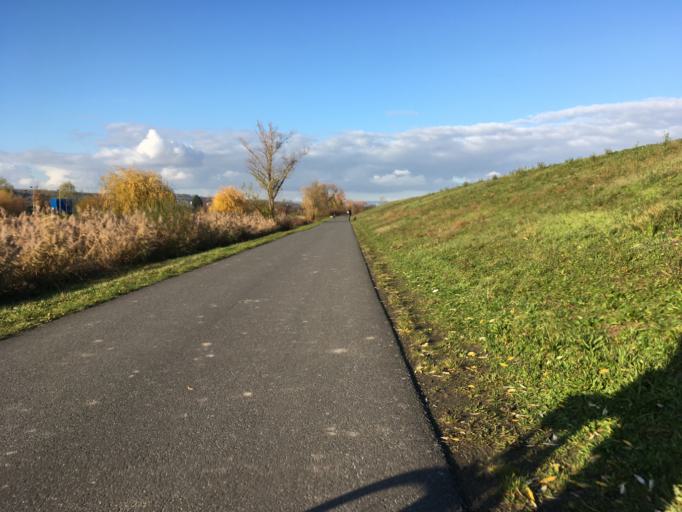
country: DE
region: Rheinland-Pfalz
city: Bodenheim
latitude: 49.9307
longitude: 8.3312
